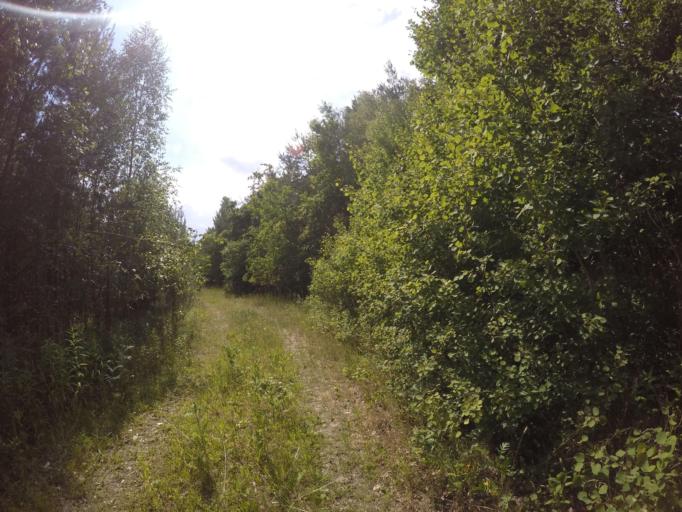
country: DE
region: Lower Saxony
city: Bleckede
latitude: 53.2565
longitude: 10.7266
